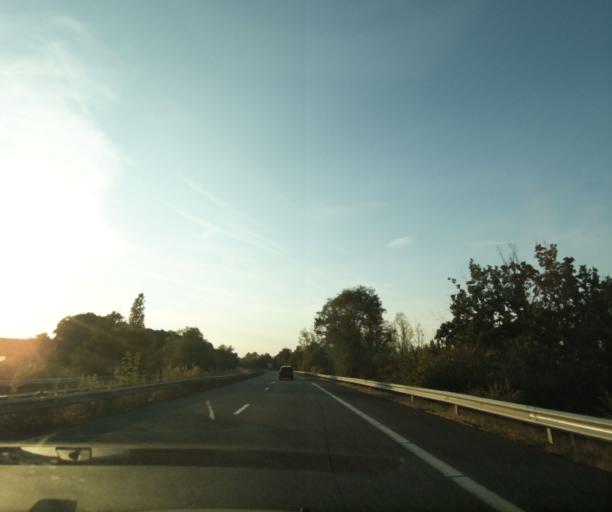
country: FR
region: Aquitaine
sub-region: Departement du Lot-et-Garonne
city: Layrac
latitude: 44.1194
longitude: 0.7204
